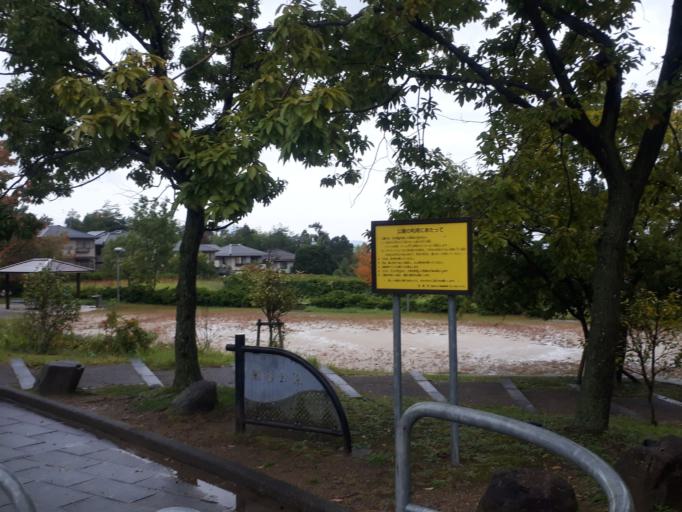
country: JP
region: Kyoto
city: Muko
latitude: 34.9840
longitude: 135.6764
